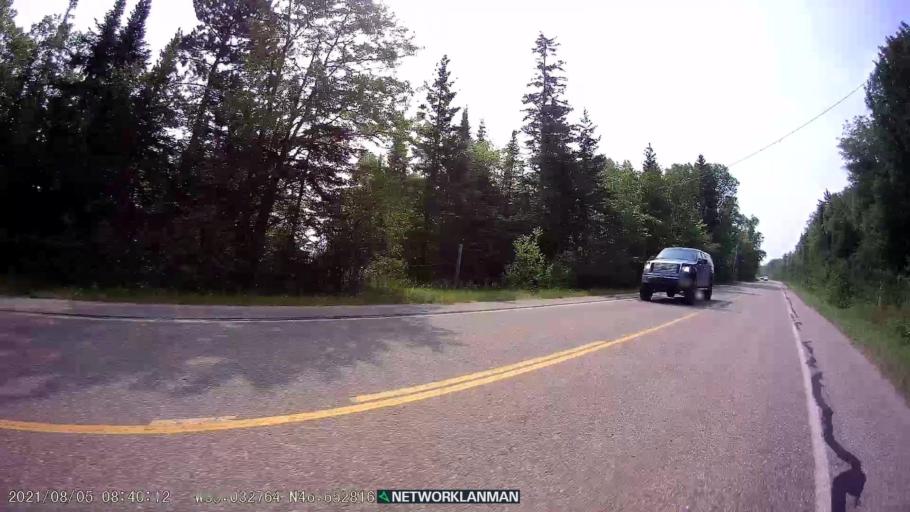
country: US
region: Michigan
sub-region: Luce County
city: Newberry
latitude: 46.6522
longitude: -85.0330
